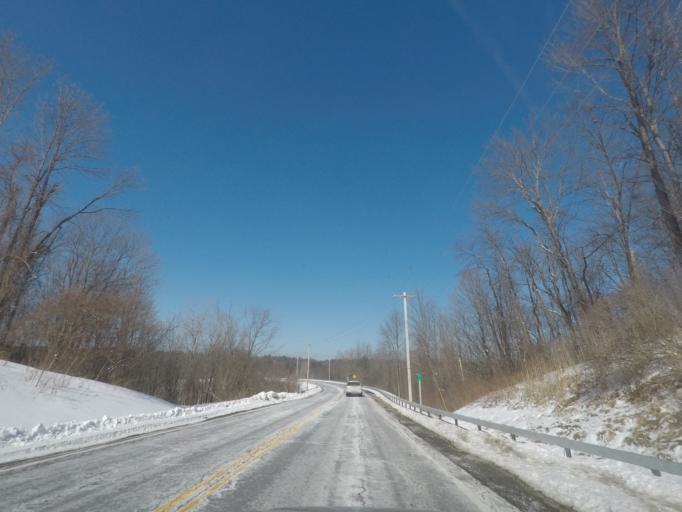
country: US
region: New York
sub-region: Saratoga County
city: Ballston Spa
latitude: 42.9940
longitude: -73.8005
